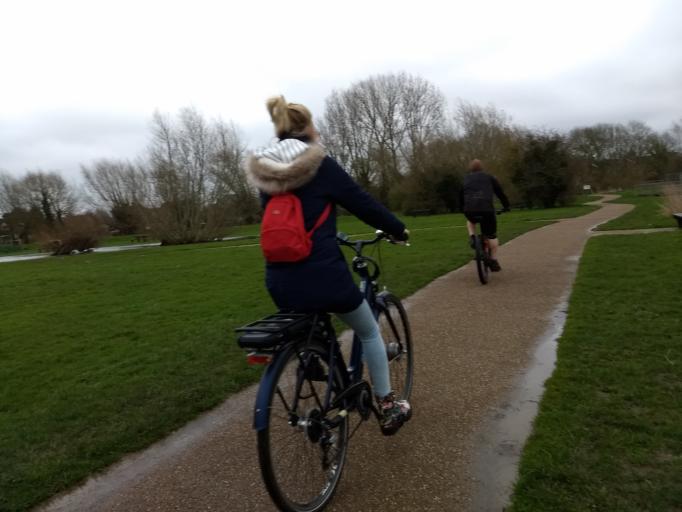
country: GB
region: England
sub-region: Milton Keynes
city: Stony Stratford
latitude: 52.0533
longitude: -0.8570
